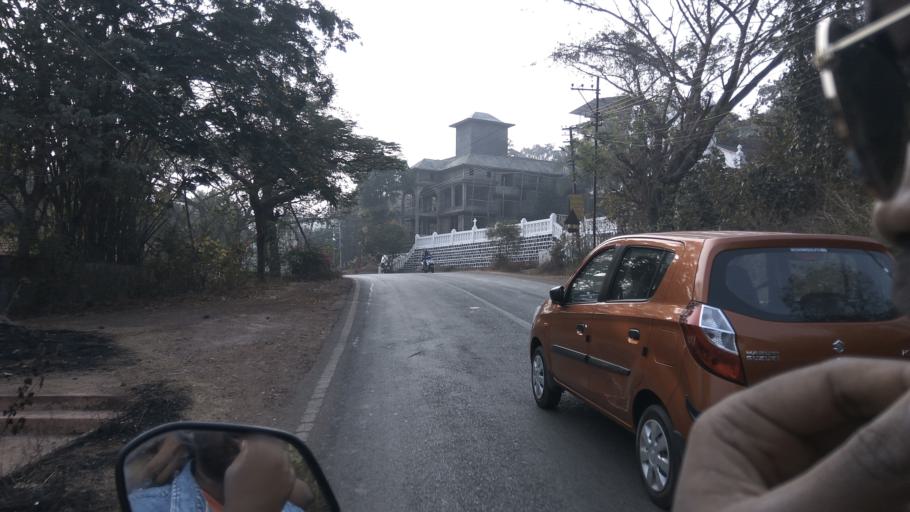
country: IN
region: Goa
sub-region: North Goa
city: Saligao
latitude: 15.5450
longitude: 73.8058
